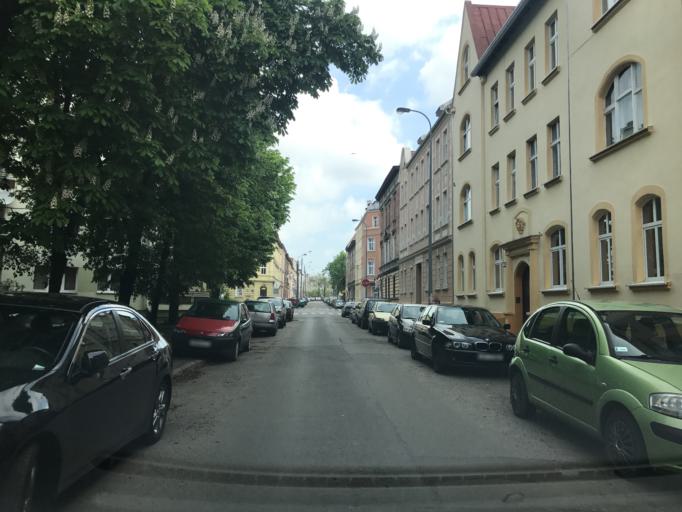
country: PL
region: Kujawsko-Pomorskie
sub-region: Bydgoszcz
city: Bydgoszcz
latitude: 53.1275
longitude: 17.9885
